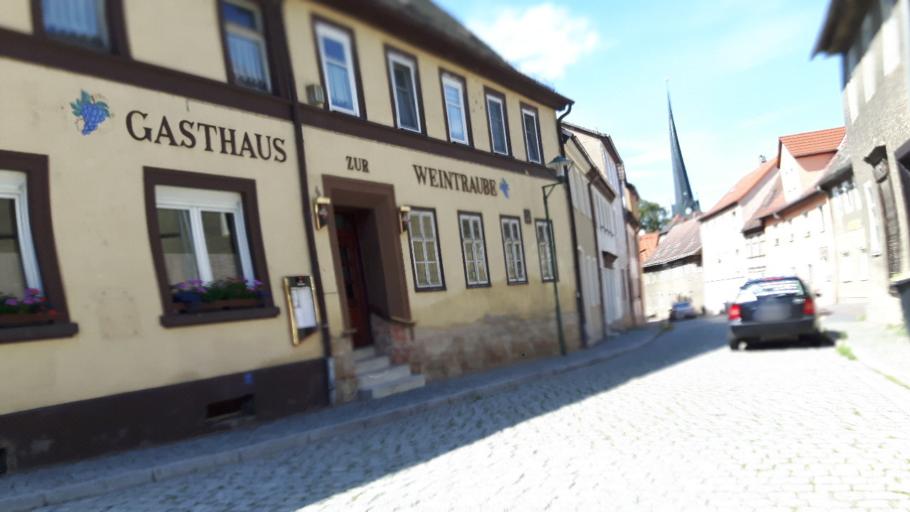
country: DE
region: Thuringia
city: Camburg
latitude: 51.0542
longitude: 11.7073
